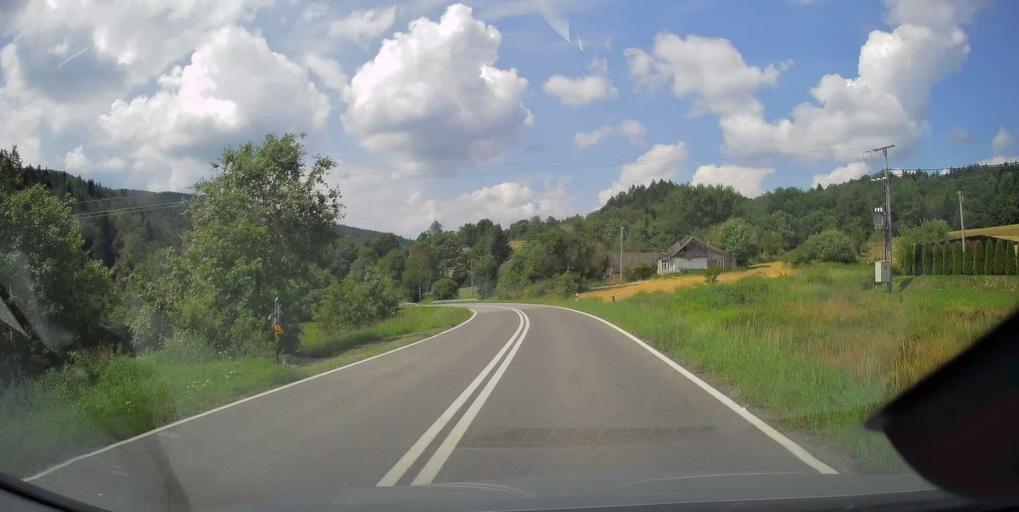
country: PL
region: Lesser Poland Voivodeship
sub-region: Powiat tarnowski
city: Zakliczyn
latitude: 49.7870
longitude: 20.7932
